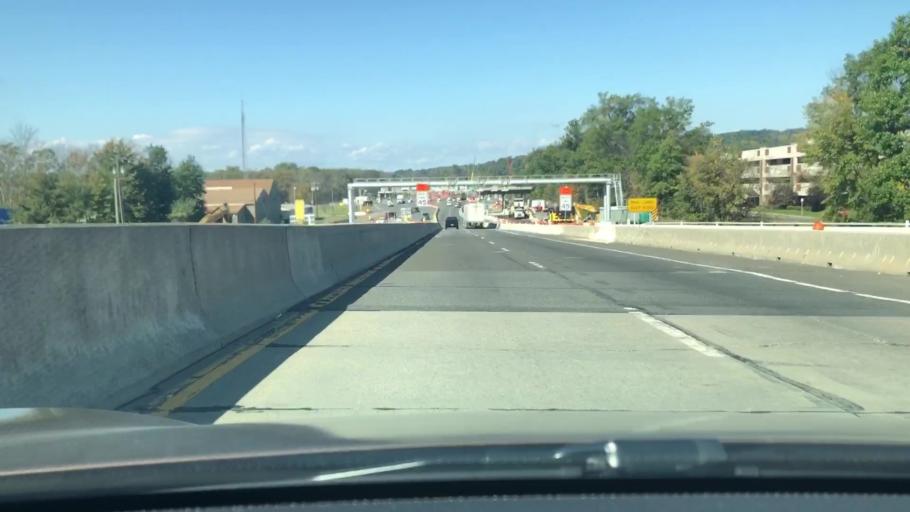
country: US
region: New York
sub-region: Orange County
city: Central Valley
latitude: 41.3118
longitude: -74.1236
